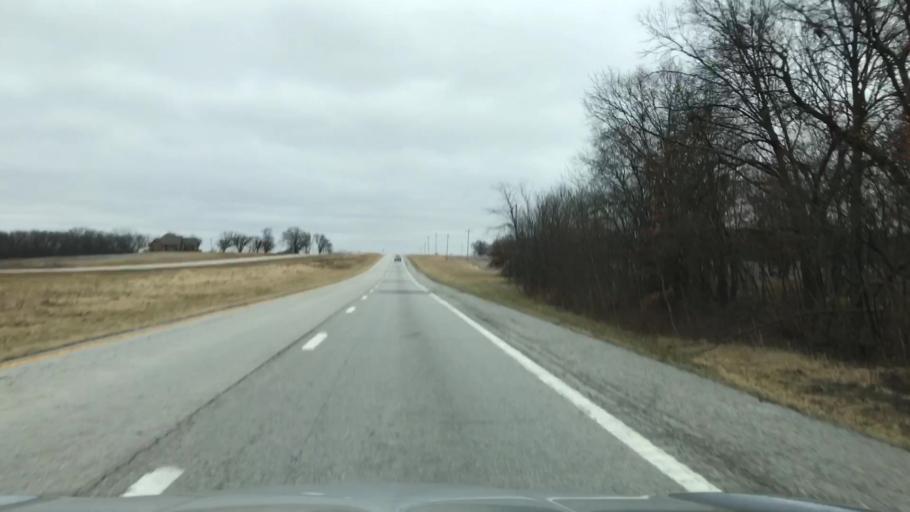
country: US
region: Missouri
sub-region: Linn County
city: Linneus
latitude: 39.7776
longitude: -93.2656
